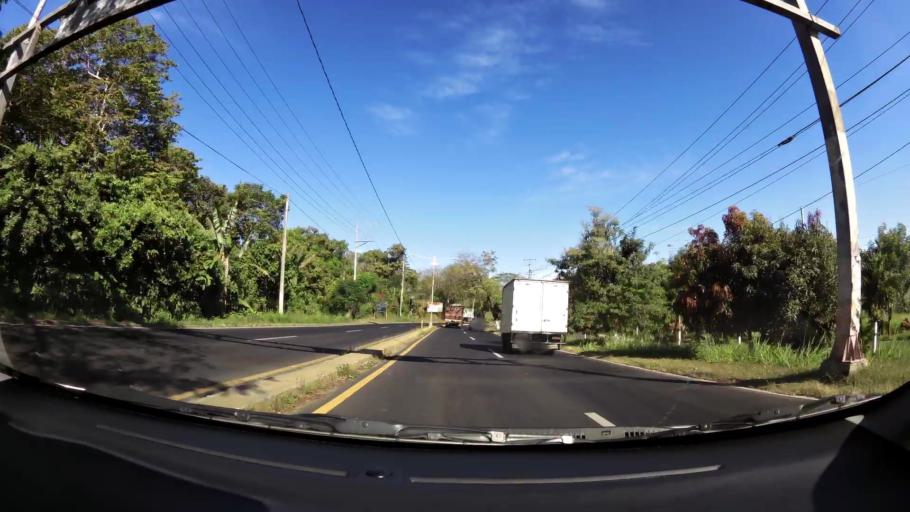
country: SV
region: Santa Ana
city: Santa Ana
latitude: 13.9584
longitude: -89.5687
